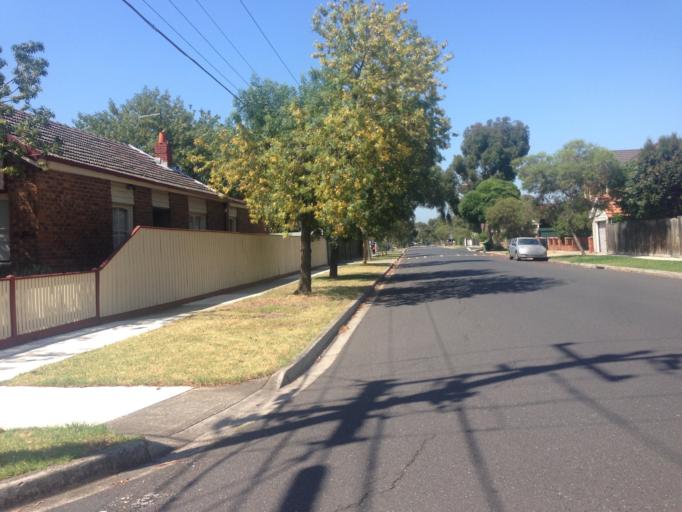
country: AU
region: Victoria
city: Thornbury
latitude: -37.7528
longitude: 144.9878
